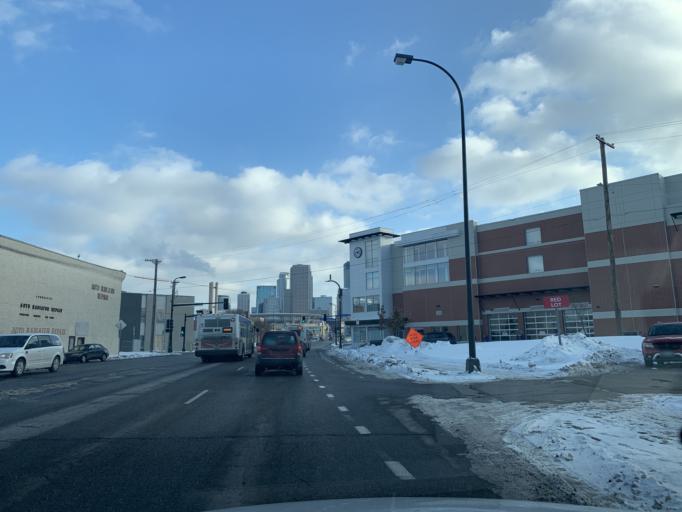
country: US
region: Minnesota
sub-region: Hennepin County
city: Minneapolis
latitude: 44.9862
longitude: -93.2865
